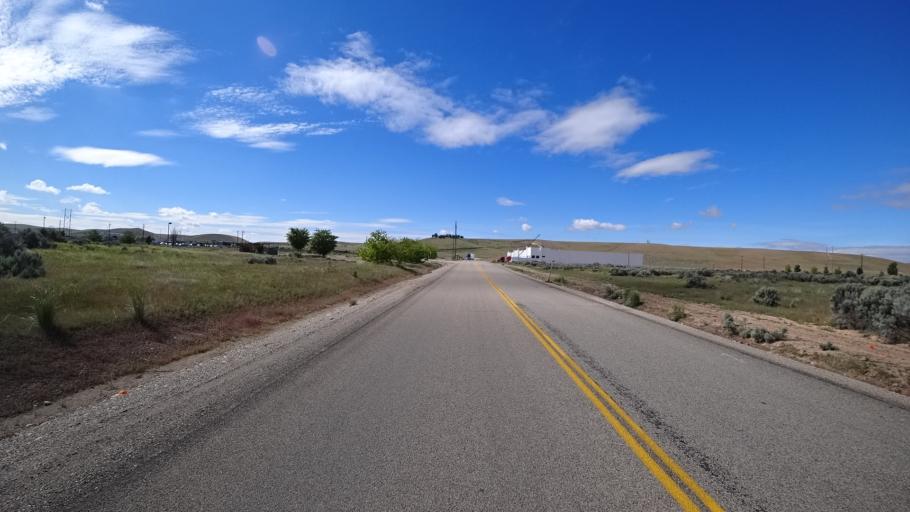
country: US
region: Idaho
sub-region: Ada County
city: Boise
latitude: 43.5187
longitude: -116.1514
